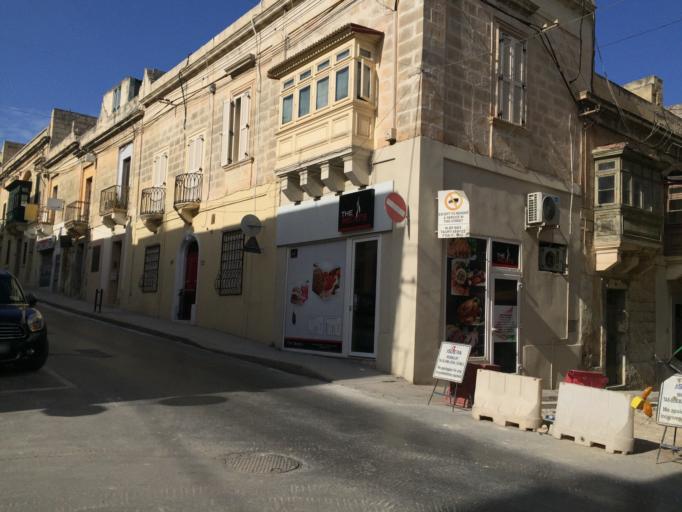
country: MT
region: Tas-Sliema
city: Sliema
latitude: 35.9102
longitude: 14.5014
